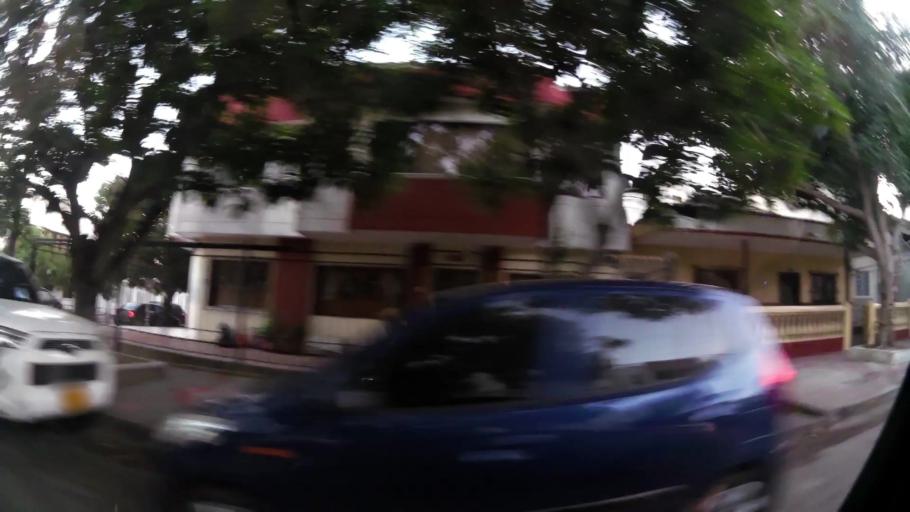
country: CO
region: Atlantico
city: Barranquilla
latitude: 10.9782
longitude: -74.8097
